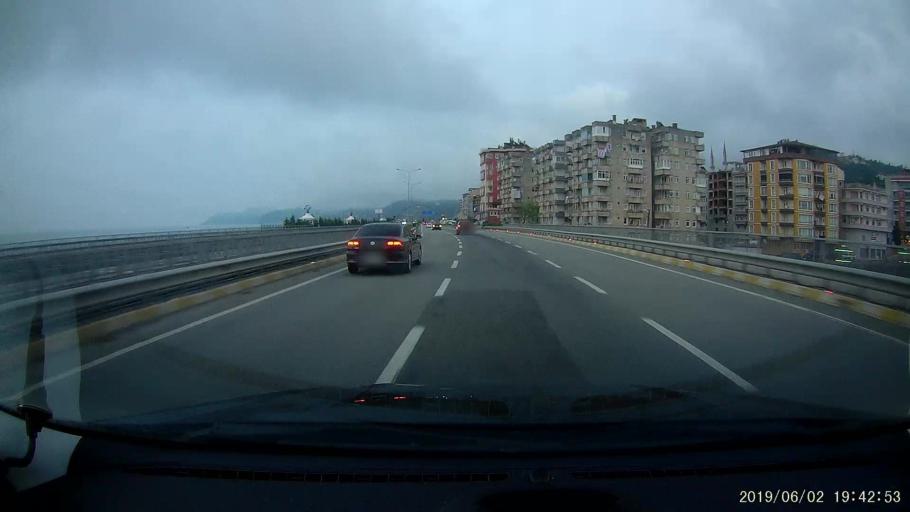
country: TR
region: Giresun
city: Kesap
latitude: 40.9169
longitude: 38.5152
